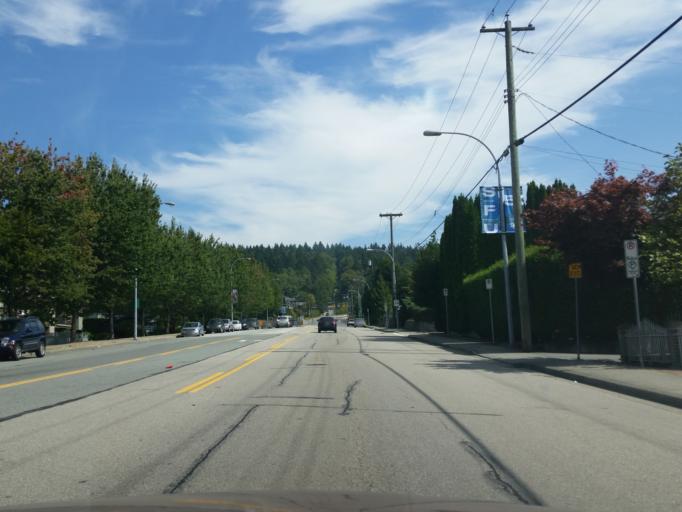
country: CA
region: British Columbia
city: Burnaby
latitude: 49.2804
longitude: -122.9569
